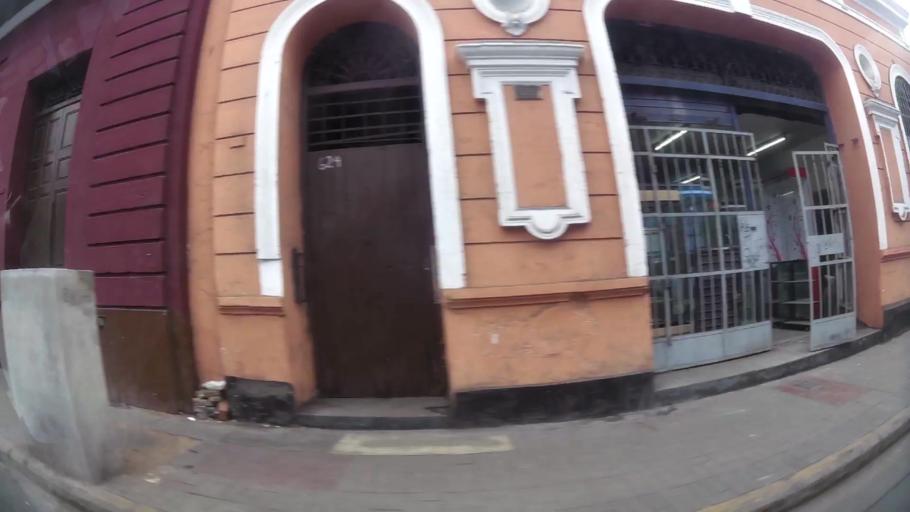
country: PE
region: Lima
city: Lima
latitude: -12.0470
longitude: -77.0248
